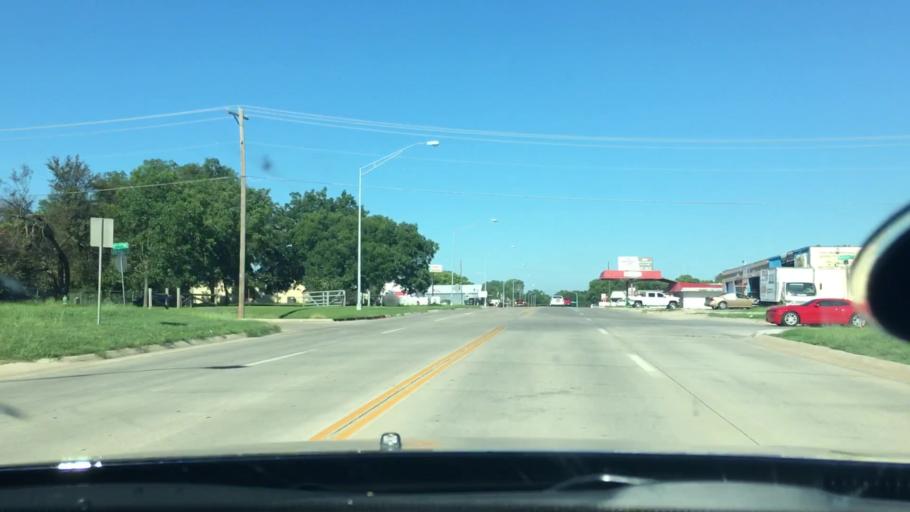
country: US
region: Oklahoma
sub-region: Carter County
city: Ardmore
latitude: 34.1854
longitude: -97.1174
